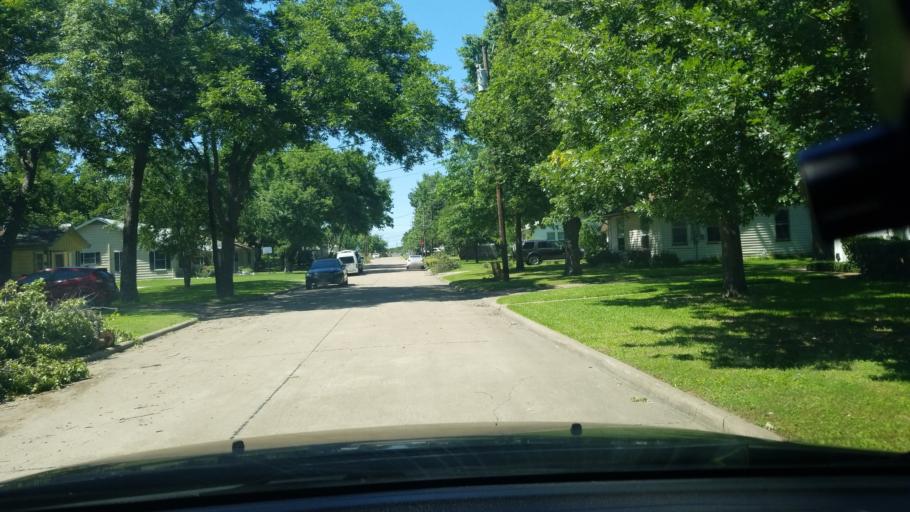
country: US
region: Texas
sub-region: Dallas County
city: Mesquite
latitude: 32.7629
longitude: -96.6034
